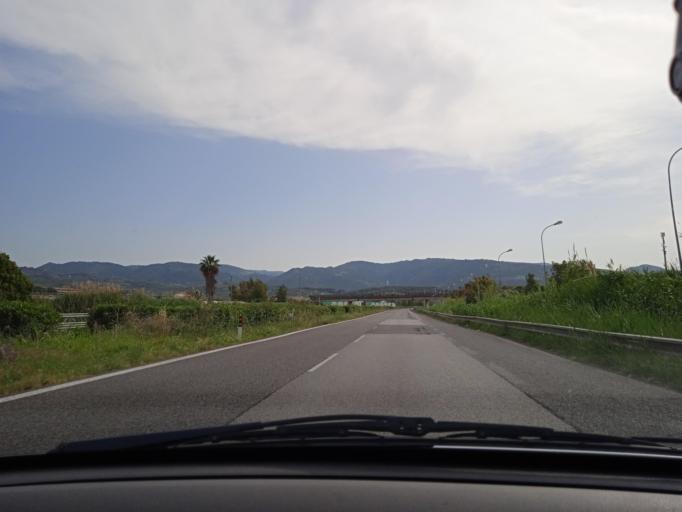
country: IT
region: Sicily
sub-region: Messina
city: Tonnarella
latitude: 38.1187
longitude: 15.1134
